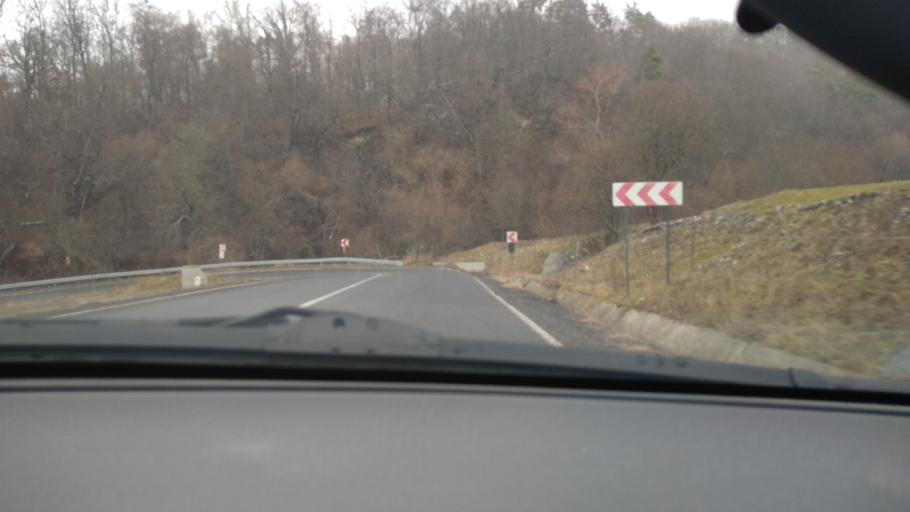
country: RO
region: Mures
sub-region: Comuna Magherani
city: Magherani
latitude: 46.5813
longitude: 24.9463
